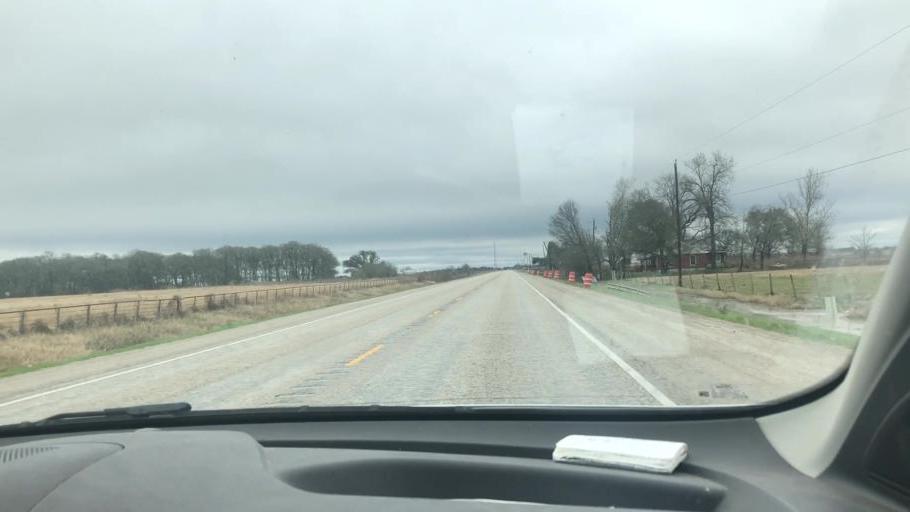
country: US
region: Texas
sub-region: Wharton County
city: Wharton
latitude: 29.2470
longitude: -96.0459
